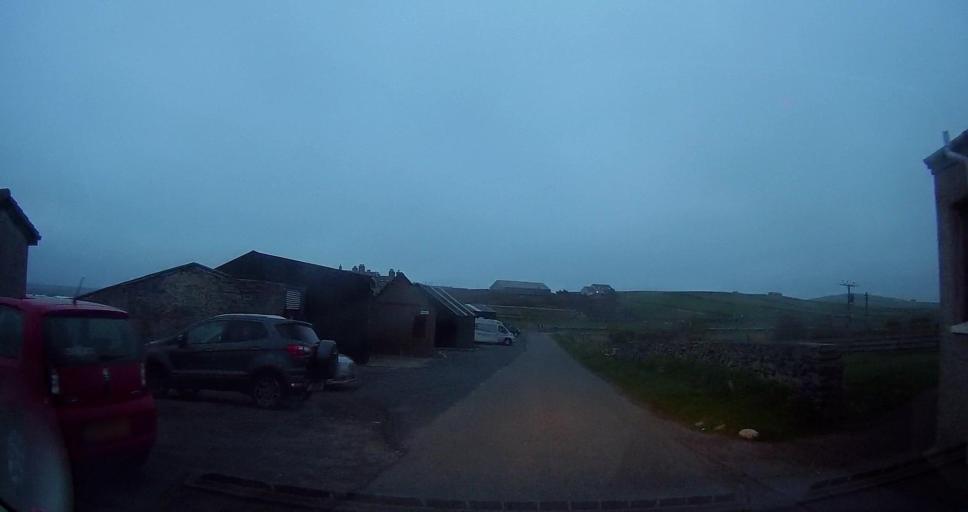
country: GB
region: Scotland
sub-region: Shetland Islands
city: Sandwick
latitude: 60.0068
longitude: -1.2226
